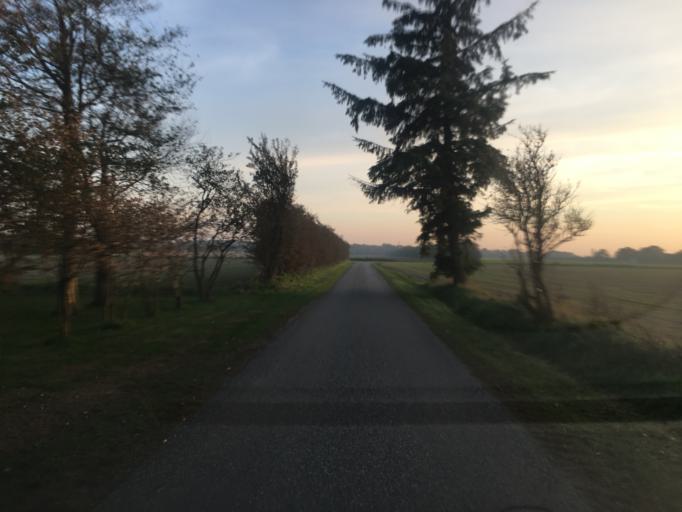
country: DK
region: South Denmark
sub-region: Aabenraa Kommune
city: Tinglev
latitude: 55.0189
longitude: 9.1275
